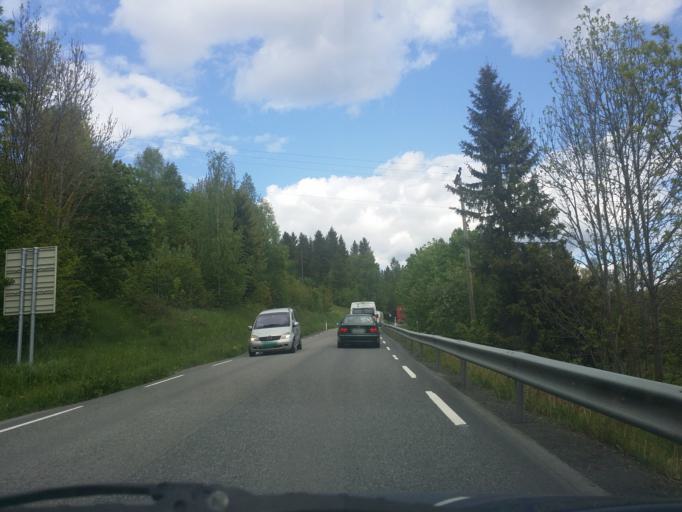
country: NO
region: Oppland
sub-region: Jevnaker
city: Jevnaker
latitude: 60.2639
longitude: 10.4558
